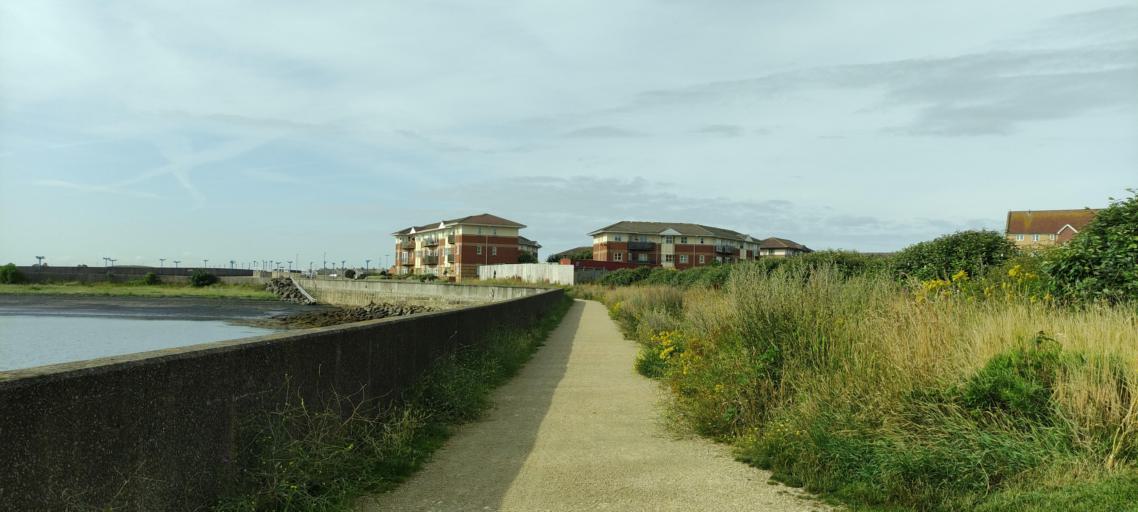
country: GB
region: England
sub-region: Hartlepool
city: Hartlepool
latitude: 54.6878
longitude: -1.1981
